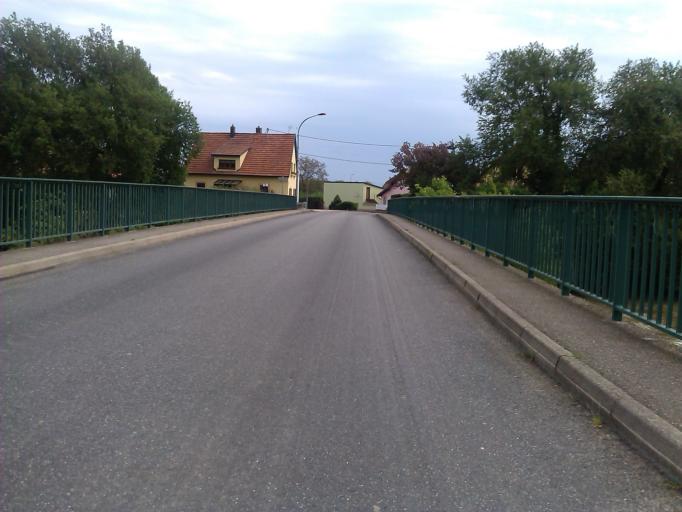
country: FR
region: Alsace
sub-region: Departement du Haut-Rhin
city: Meyenheim
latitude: 47.9119
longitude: 7.3576
